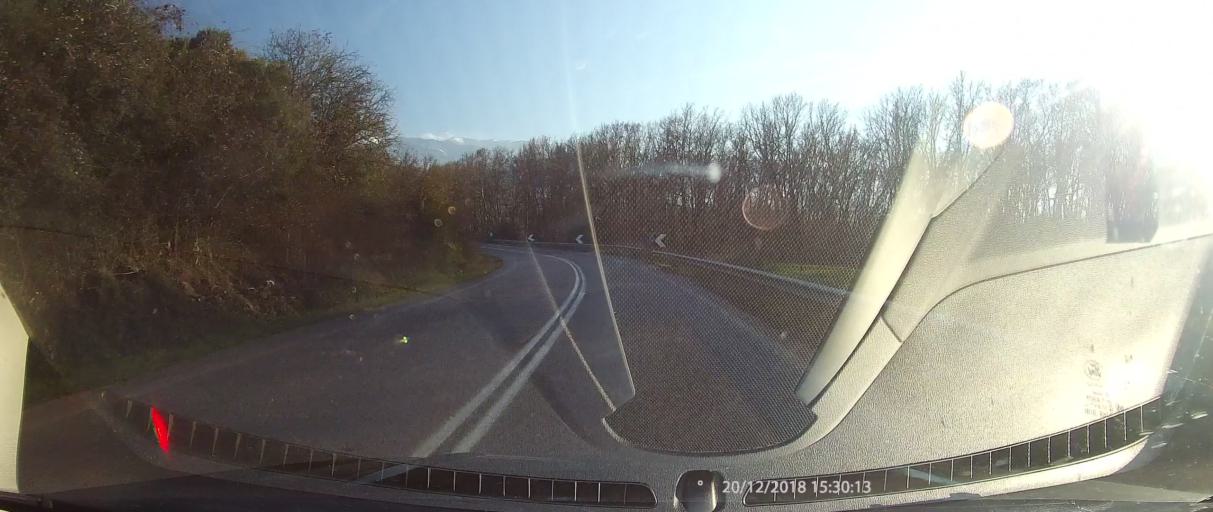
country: GR
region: Central Greece
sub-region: Nomos Fthiotidos
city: Lianokladhion
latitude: 38.9390
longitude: 22.2219
